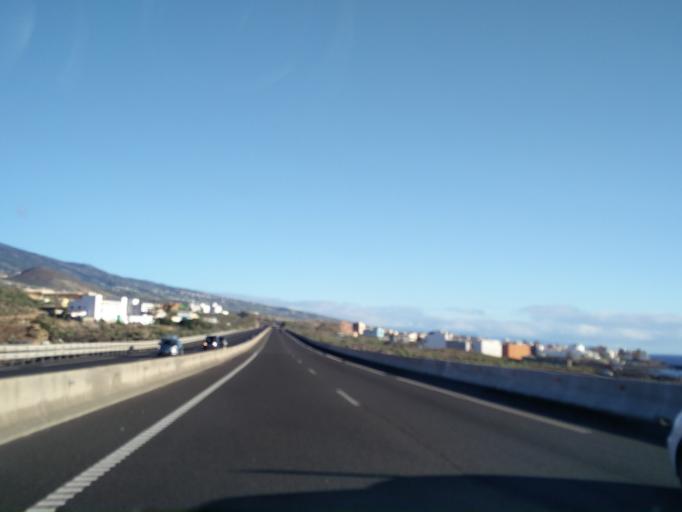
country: ES
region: Canary Islands
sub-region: Provincia de Santa Cruz de Tenerife
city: Fasnia
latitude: 28.1873
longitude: -16.4285
